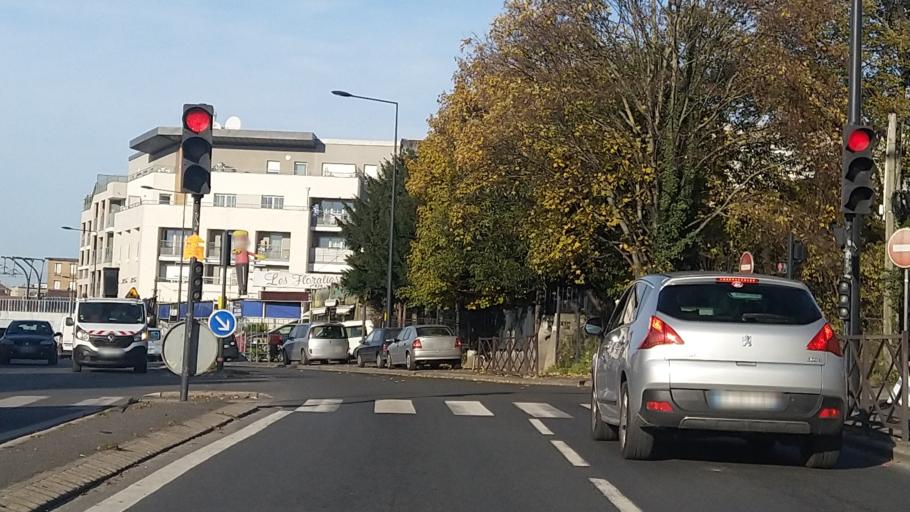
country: FR
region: Ile-de-France
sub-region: Departement de Seine-Saint-Denis
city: Stains
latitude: 48.9567
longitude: 2.3832
